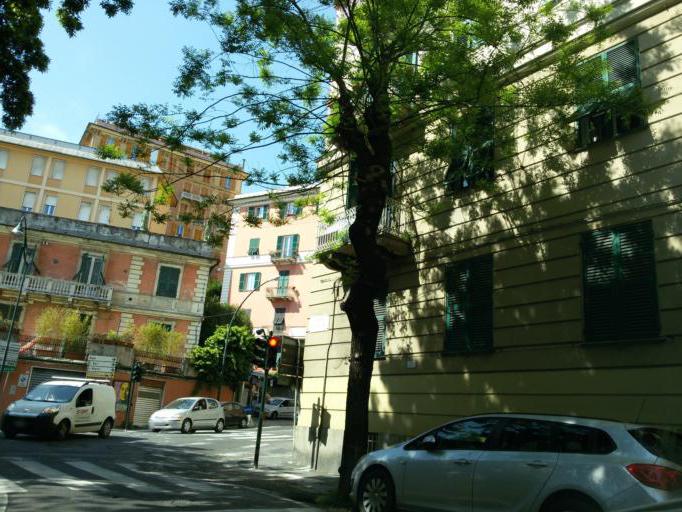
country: IT
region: Liguria
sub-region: Provincia di Genova
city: Genoa
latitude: 44.4204
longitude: 8.9257
